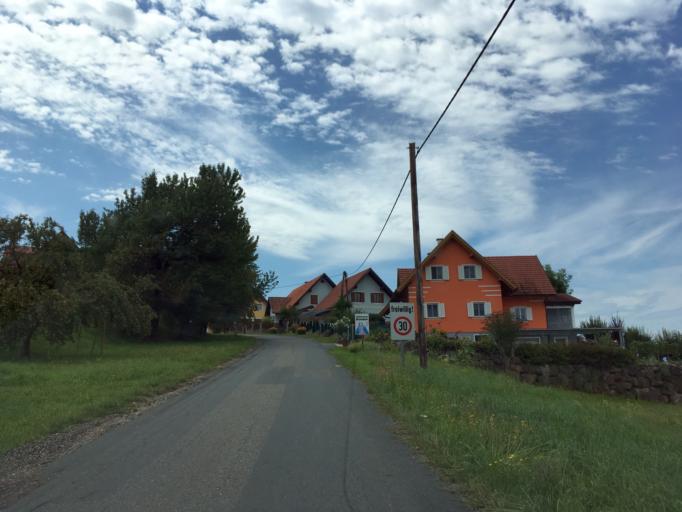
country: AT
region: Styria
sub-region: Politischer Bezirk Leibnitz
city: Kitzeck im Sausal
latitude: 46.7881
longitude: 15.4039
